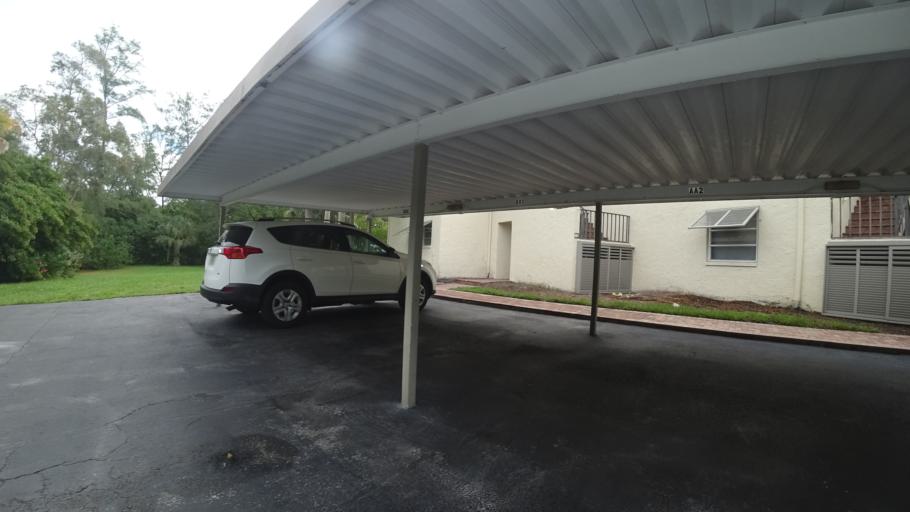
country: US
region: Florida
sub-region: Manatee County
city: Longboat Key
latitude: 27.3927
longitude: -82.6410
